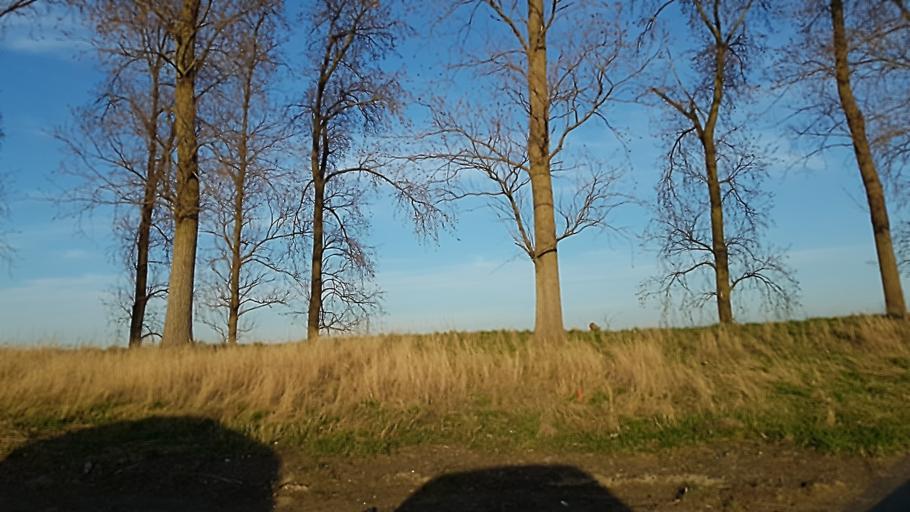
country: NL
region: North Brabant
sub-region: Gemeente Woensdrecht
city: Woensdrecht
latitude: 51.3943
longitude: 4.2776
